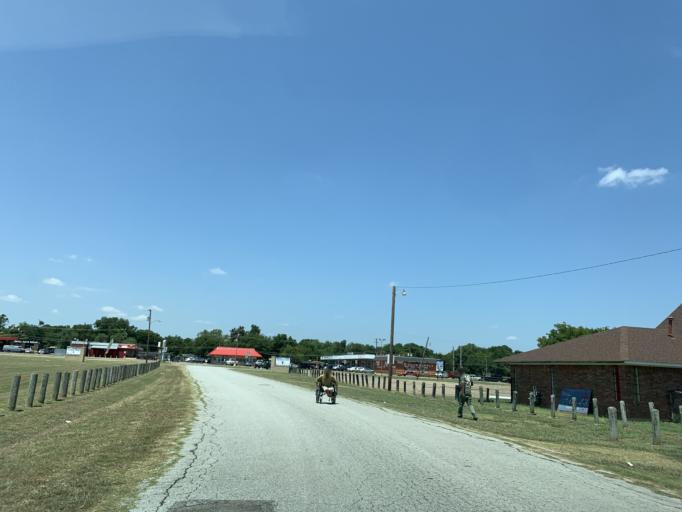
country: US
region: Texas
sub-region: Dallas County
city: Hutchins
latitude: 32.6954
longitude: -96.7654
